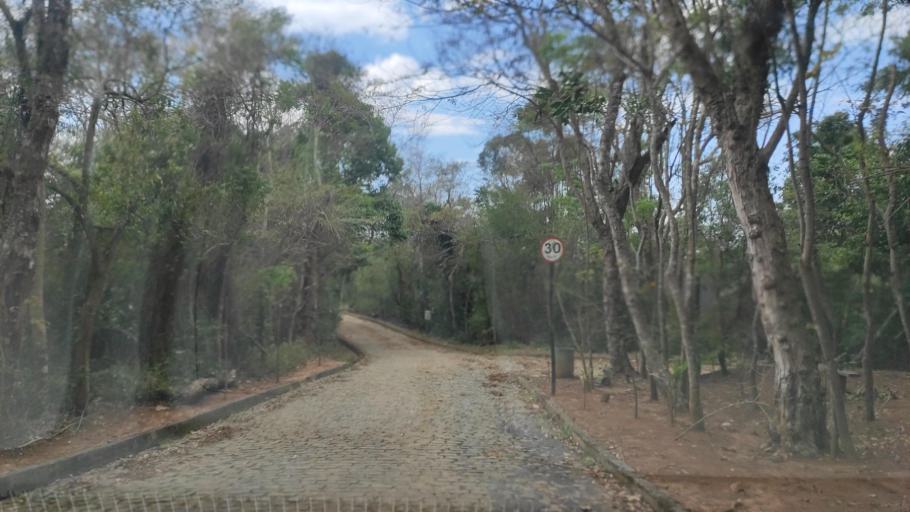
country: BR
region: Espirito Santo
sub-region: Vitoria
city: Vitoria
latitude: -20.3072
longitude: -40.3411
